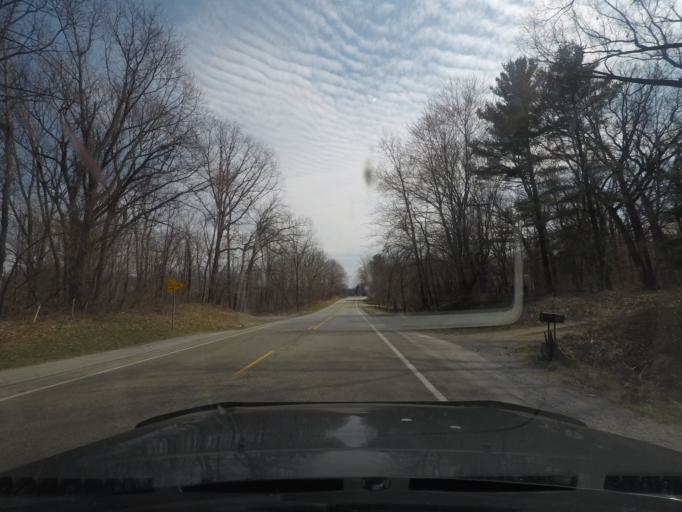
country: US
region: Indiana
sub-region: LaPorte County
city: Trail Creek
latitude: 41.6864
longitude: -86.7972
